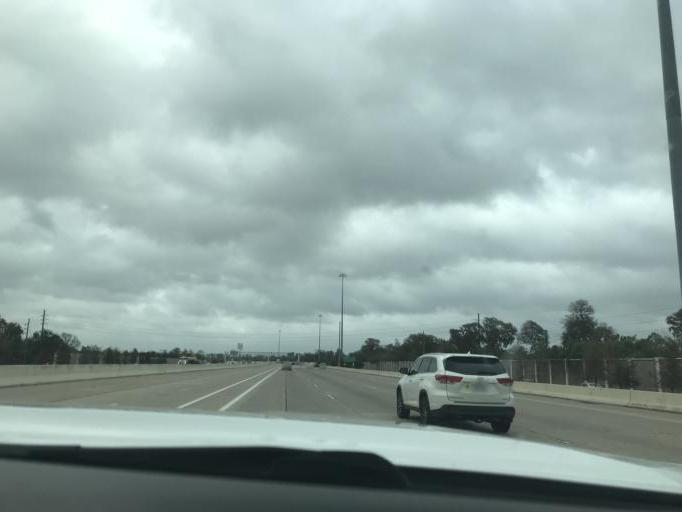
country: US
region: Texas
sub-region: Fort Bend County
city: Greatwood
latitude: 29.5632
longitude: -95.6808
